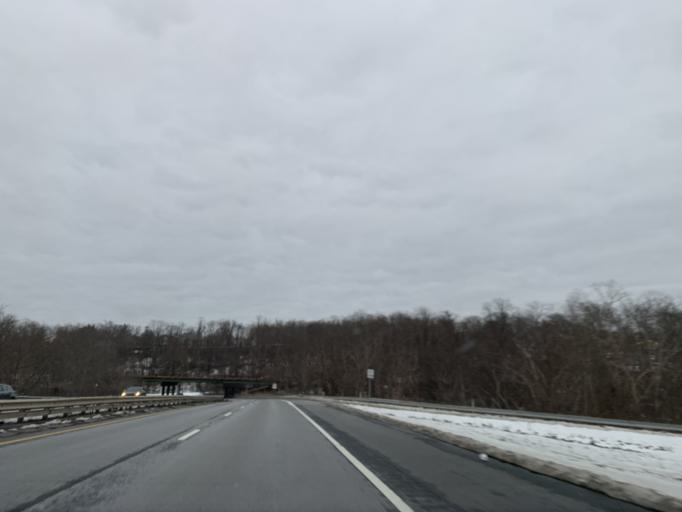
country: US
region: Massachusetts
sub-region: Bristol County
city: Fall River
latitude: 41.7291
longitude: -71.1406
